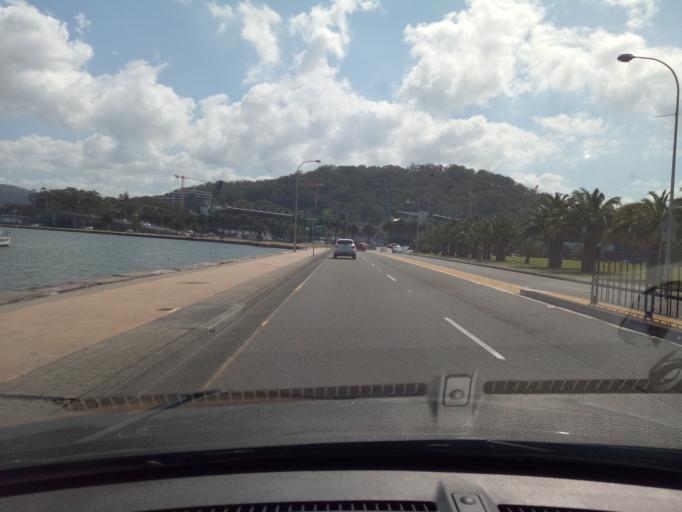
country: AU
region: New South Wales
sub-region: Gosford Shire
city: Gosford
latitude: -33.4309
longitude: 151.3393
